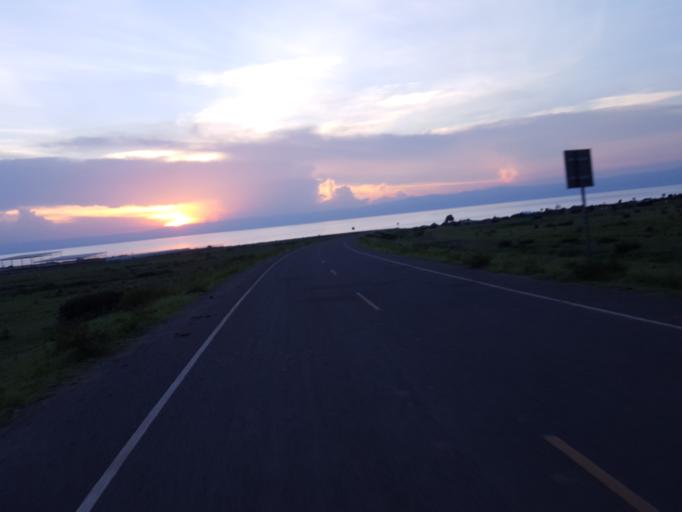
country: UG
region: Western Region
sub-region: Kibale District
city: Kagadi
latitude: 1.2537
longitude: 30.7553
